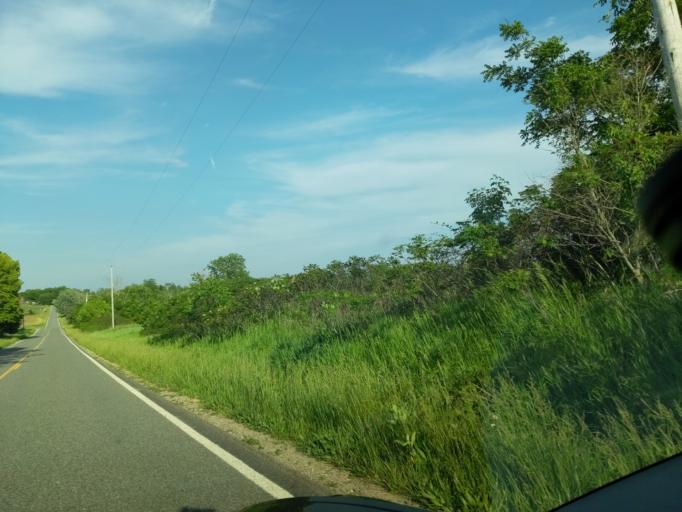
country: US
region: Michigan
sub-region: Barry County
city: Nashville
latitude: 42.6250
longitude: -85.1171
